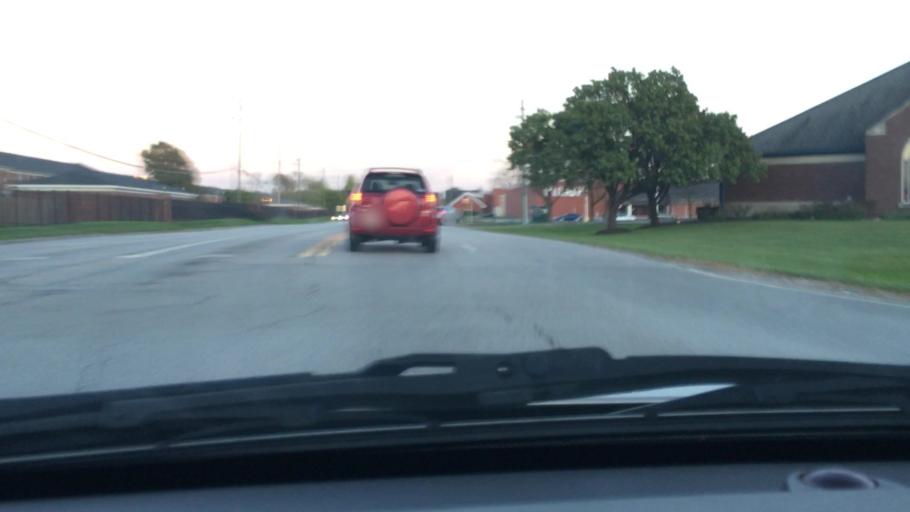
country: US
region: Indiana
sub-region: Marion County
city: Lawrence
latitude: 39.8907
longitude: -86.0460
